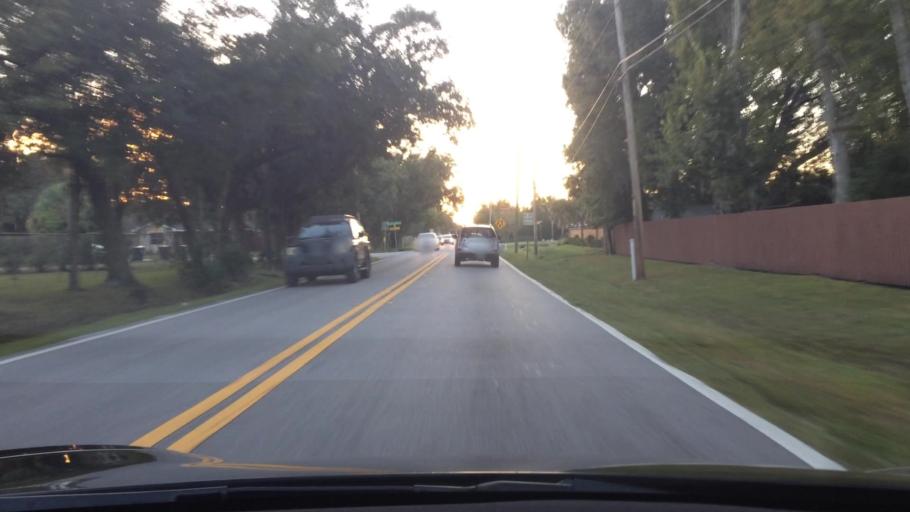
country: US
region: Florida
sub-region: Hillsborough County
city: Lutz
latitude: 28.1719
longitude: -82.4664
